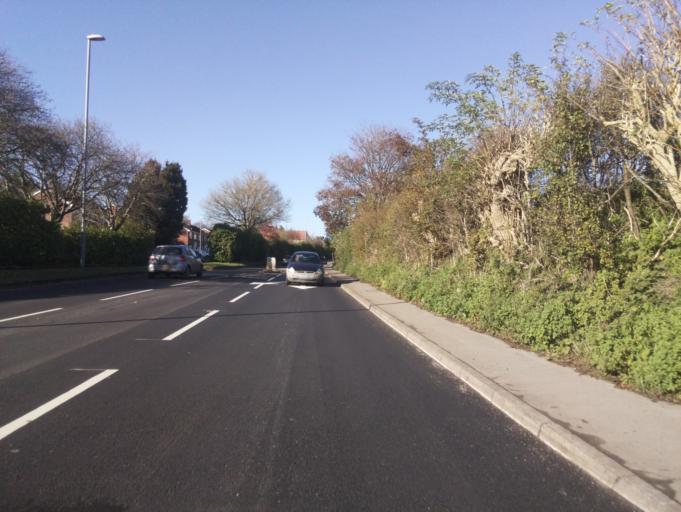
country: GB
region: England
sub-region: Dorset
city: Sherborne
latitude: 50.9456
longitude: -2.5268
